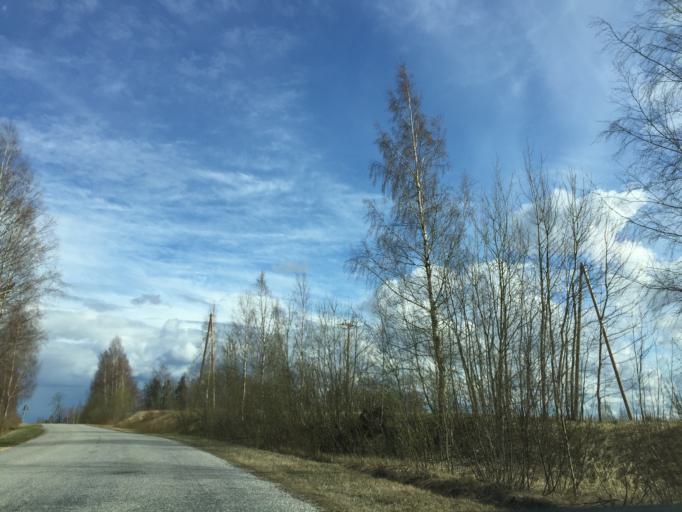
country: LV
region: Limbazu Rajons
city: Limbazi
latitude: 57.5962
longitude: 24.8283
